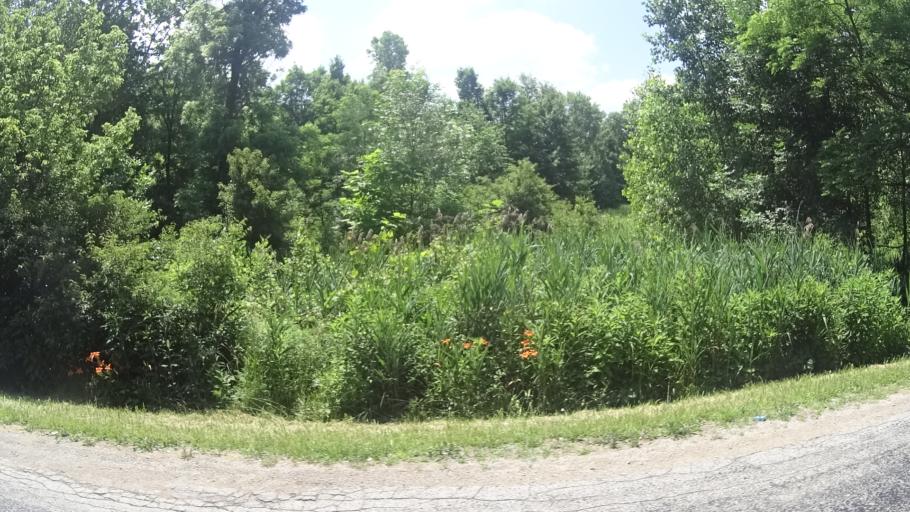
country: US
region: Ohio
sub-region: Huron County
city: Wakeman
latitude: 41.3217
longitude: -82.3628
